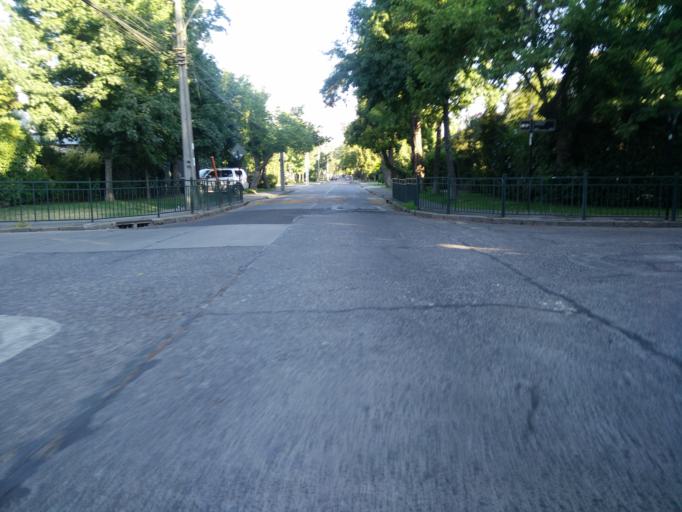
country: CL
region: Santiago Metropolitan
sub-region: Provincia de Santiago
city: Villa Presidente Frei, Nunoa, Santiago, Chile
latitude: -33.3894
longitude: -70.5923
